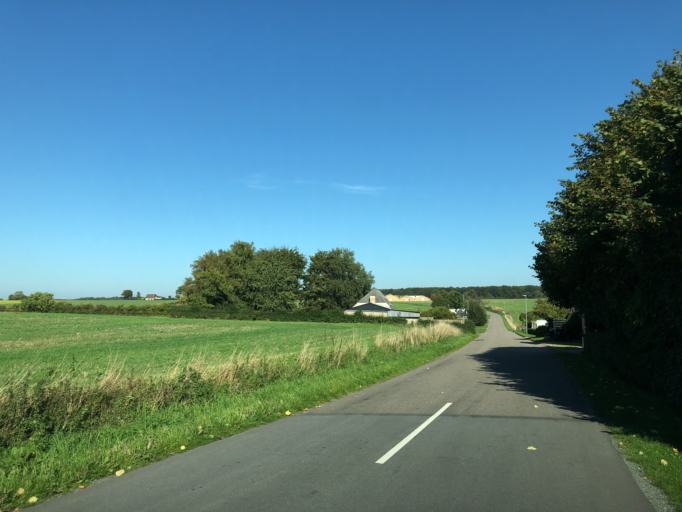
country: DK
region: South Denmark
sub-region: Sonderborg Kommune
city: Dybbol
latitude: 54.9557
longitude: 9.7292
